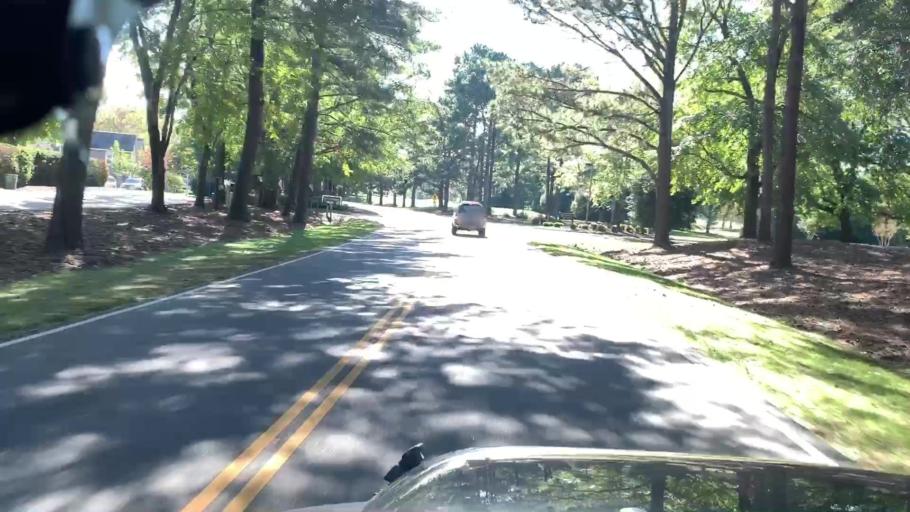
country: US
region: Virginia
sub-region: City of Williamsburg
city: Williamsburg
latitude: 37.2310
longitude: -76.6646
